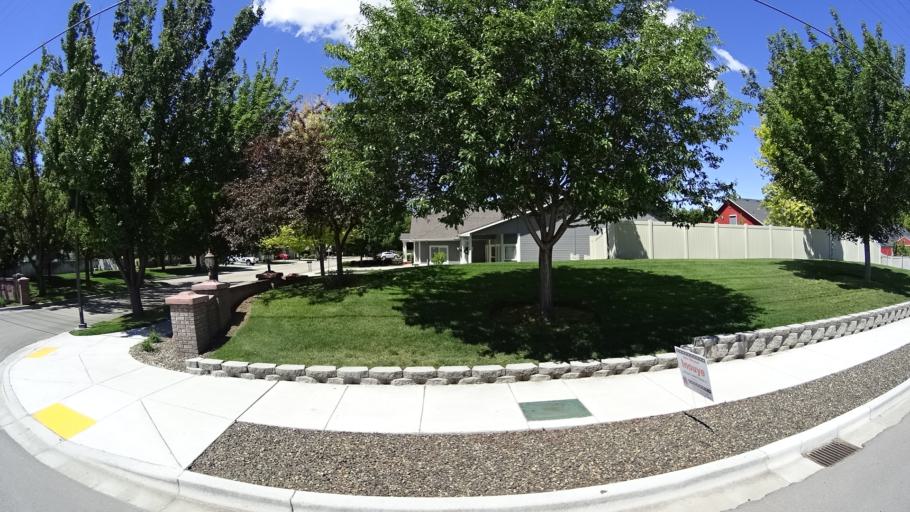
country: US
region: Idaho
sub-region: Ada County
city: Meridian
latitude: 43.6265
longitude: -116.3345
